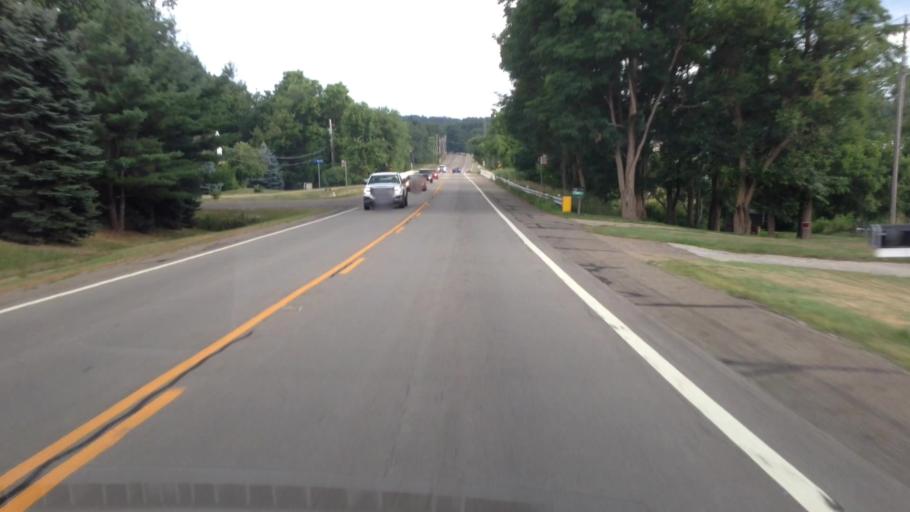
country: US
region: Ohio
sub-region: Summit County
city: Lakemore
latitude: 41.0075
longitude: -81.4637
